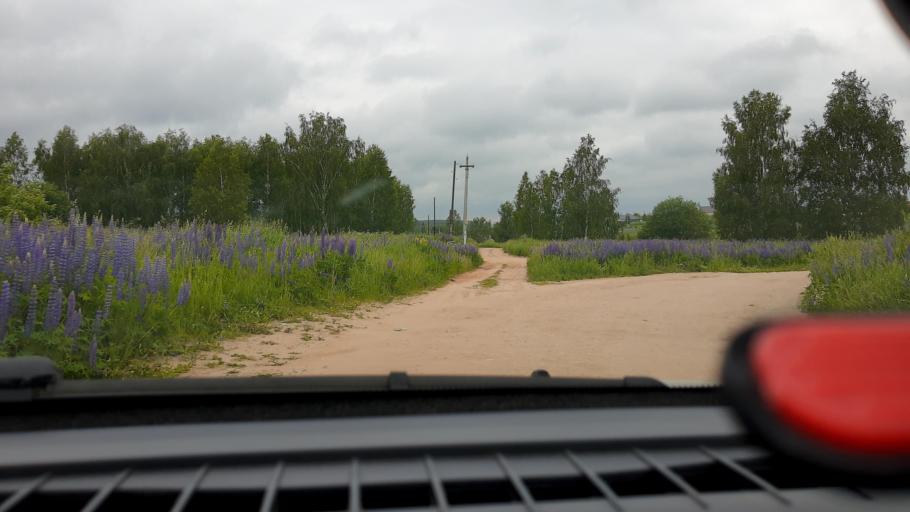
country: RU
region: Nizjnij Novgorod
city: Burevestnik
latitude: 56.1022
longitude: 43.9482
